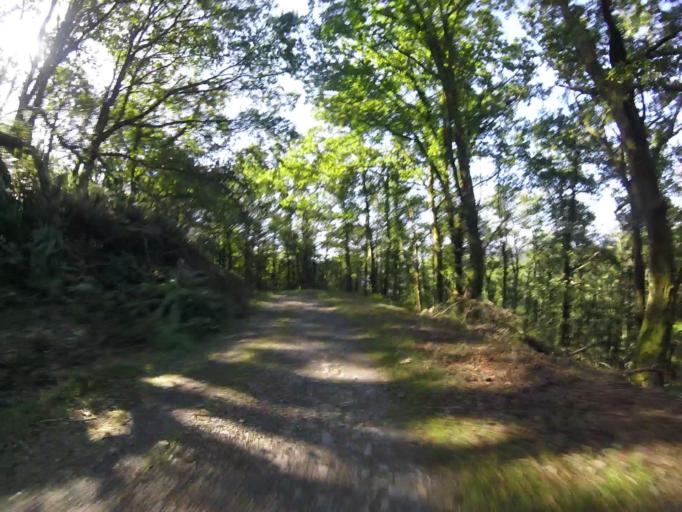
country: ES
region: Navarre
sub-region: Provincia de Navarra
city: Arano
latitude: 43.2397
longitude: -1.8875
